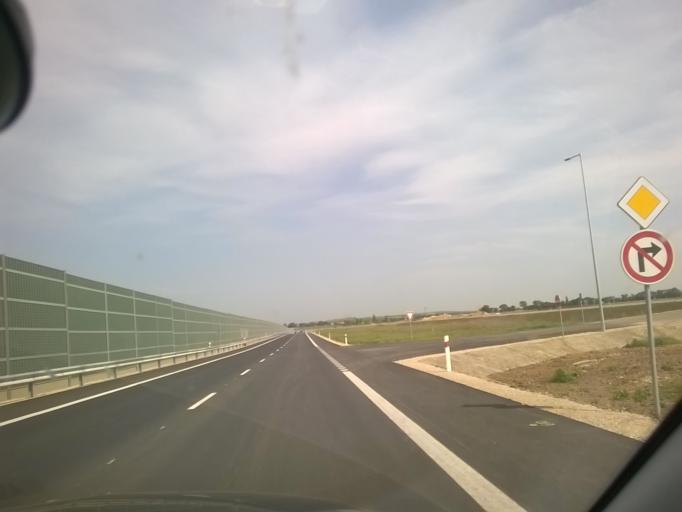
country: SK
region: Nitriansky
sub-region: Okres Nitra
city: Nitra
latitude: 48.3574
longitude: 18.0379
